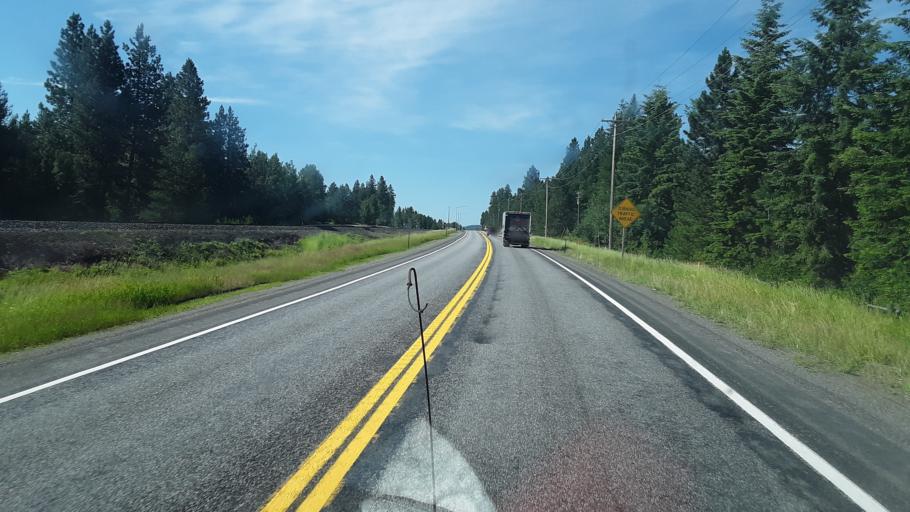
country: US
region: Idaho
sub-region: Bonner County
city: Ponderay
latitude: 48.4885
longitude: -116.4585
